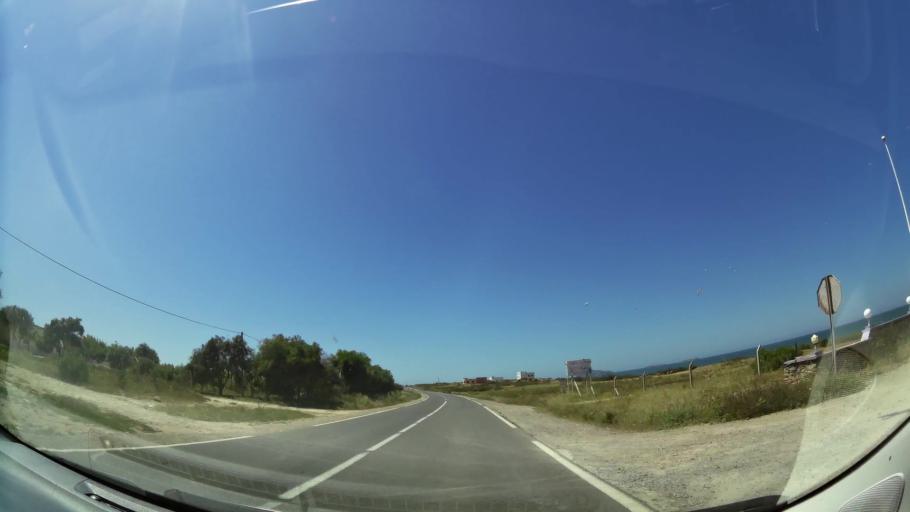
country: MA
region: Oriental
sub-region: Berkane-Taourirt
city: Madagh
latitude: 35.1248
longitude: -2.3871
